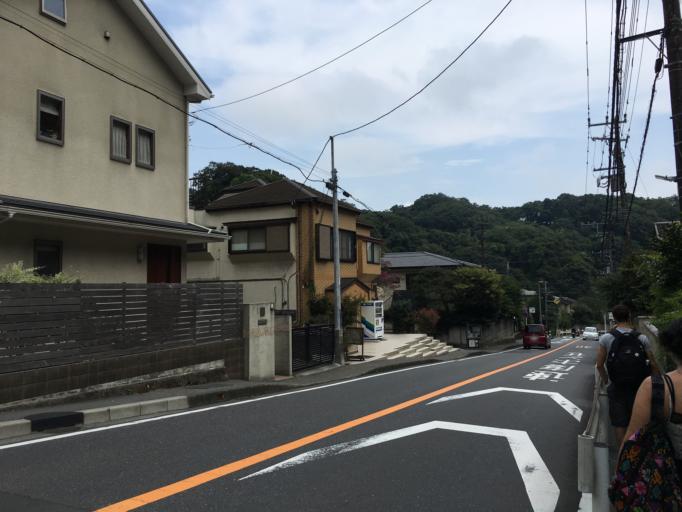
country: JP
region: Kanagawa
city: Kamakura
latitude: 35.3286
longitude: 139.5549
